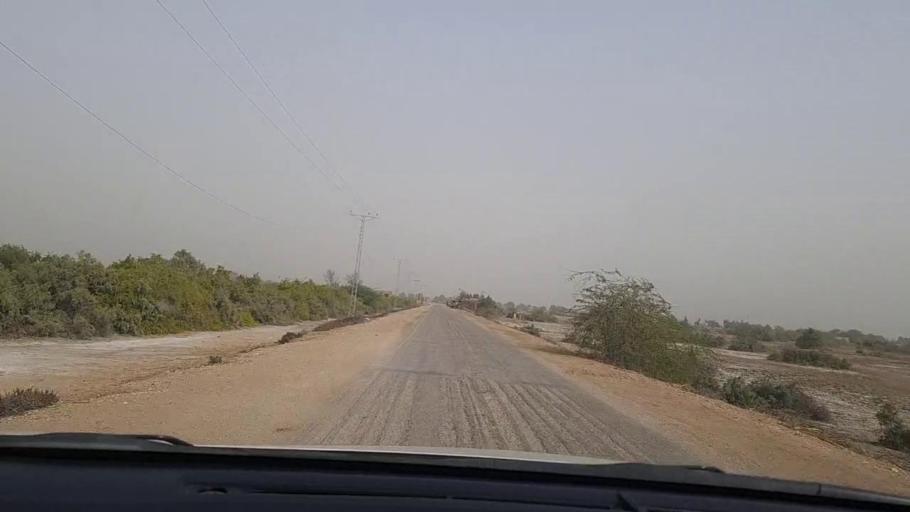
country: PK
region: Sindh
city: Samaro
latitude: 25.3826
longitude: 69.3332
